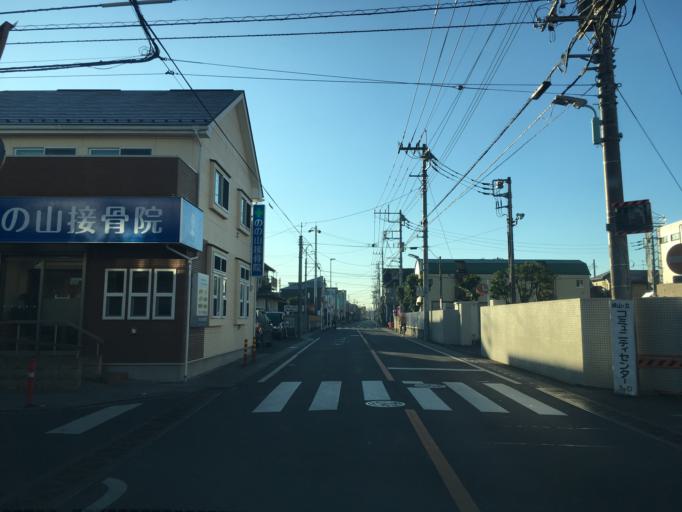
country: JP
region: Saitama
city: Sayama
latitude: 35.8082
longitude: 139.4170
